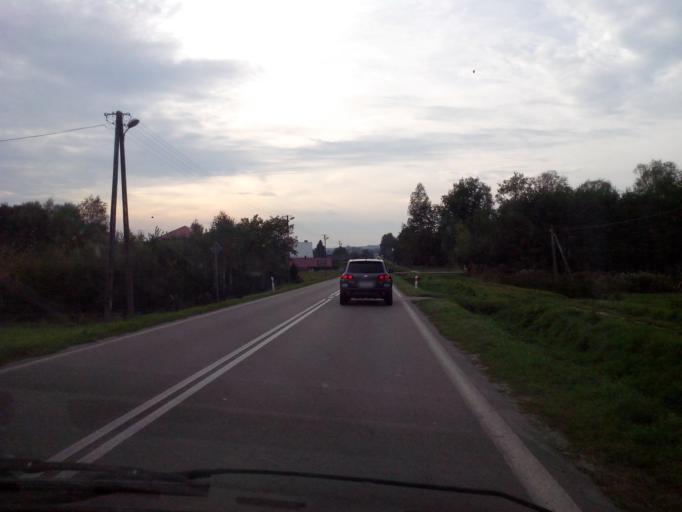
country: PL
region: Subcarpathian Voivodeship
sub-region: Powiat przeworski
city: Jawornik Polski
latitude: 49.8342
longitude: 22.2875
